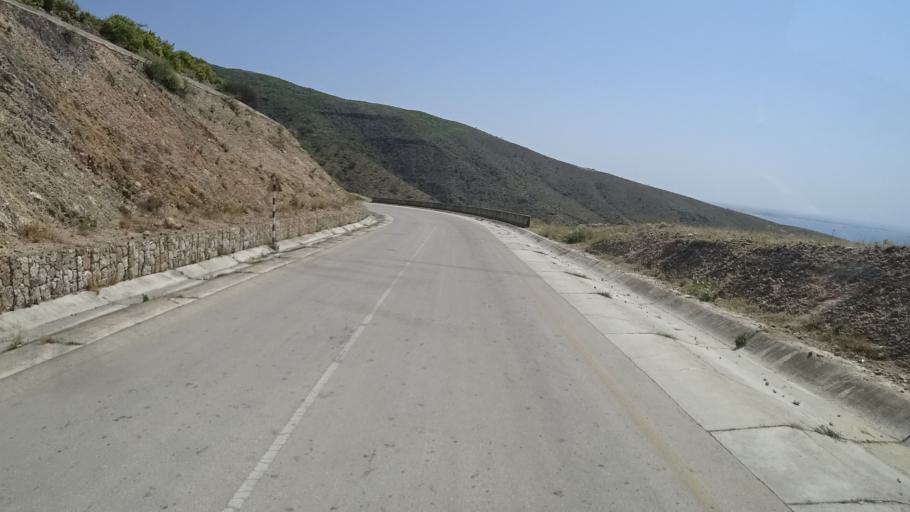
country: OM
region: Zufar
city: Salalah
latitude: 17.0477
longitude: 54.6110
